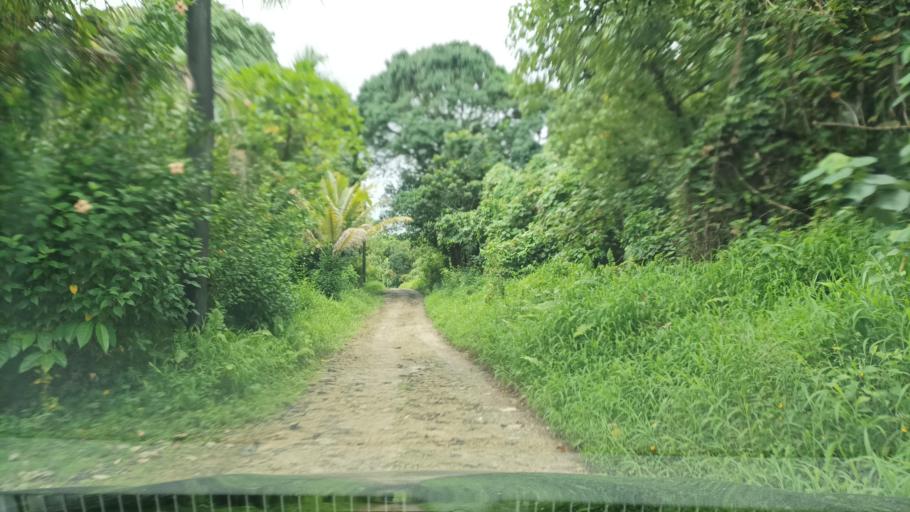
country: FM
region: Pohnpei
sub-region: Madolenihm Municipality
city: Madolenihm Municipality Government
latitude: 6.8185
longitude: 158.2843
